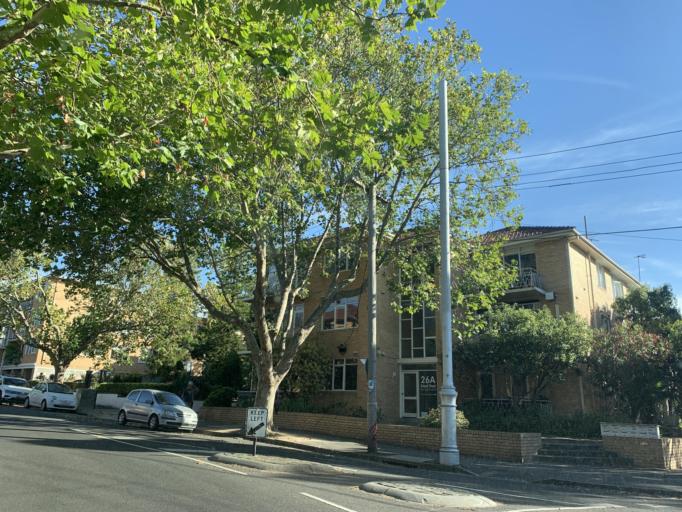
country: AU
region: Victoria
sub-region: Port Phillip
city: Saint Kilda
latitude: -37.8654
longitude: 144.9767
